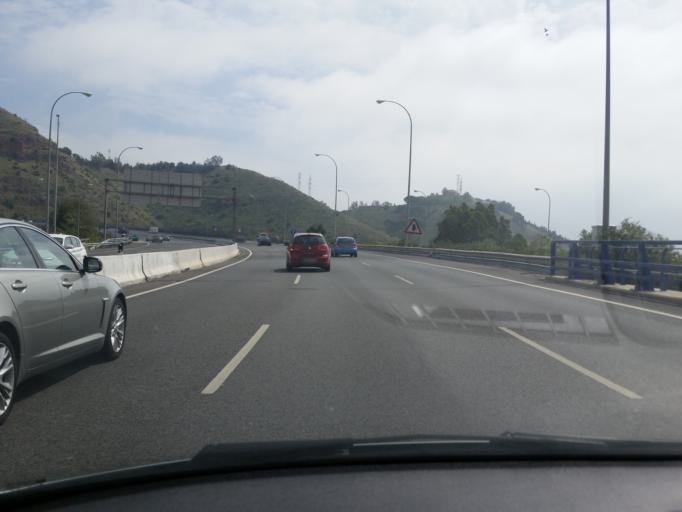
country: ES
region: Andalusia
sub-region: Provincia de Malaga
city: Malaga
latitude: 36.7388
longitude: -4.3948
